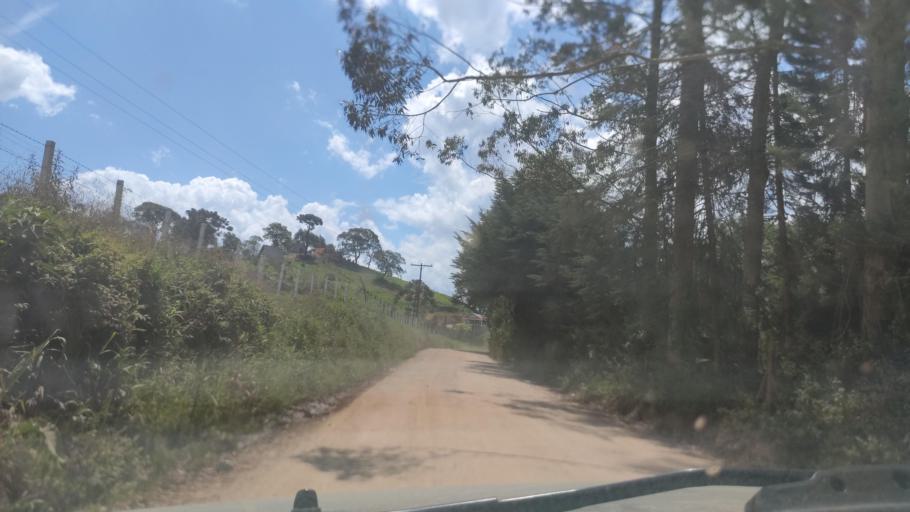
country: BR
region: Minas Gerais
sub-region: Cambui
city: Cambui
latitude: -22.7088
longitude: -46.0306
